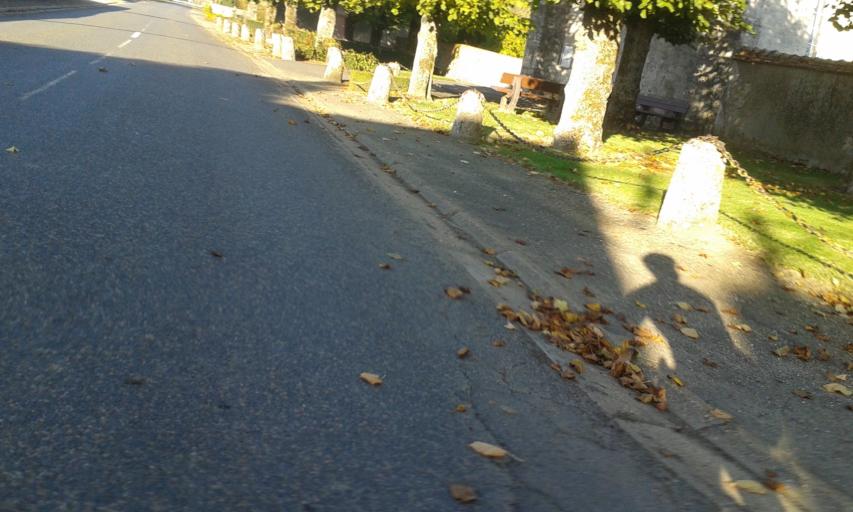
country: FR
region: Centre
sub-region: Departement du Loir-et-Cher
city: Oucques
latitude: 47.8887
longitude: 1.3710
